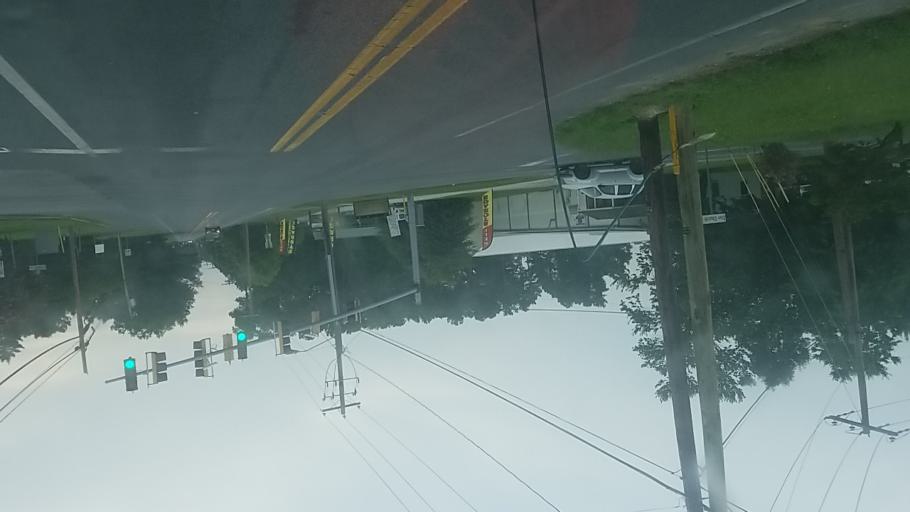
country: US
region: Maryland
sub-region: Wicomico County
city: Salisbury
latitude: 38.3772
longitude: -75.5242
